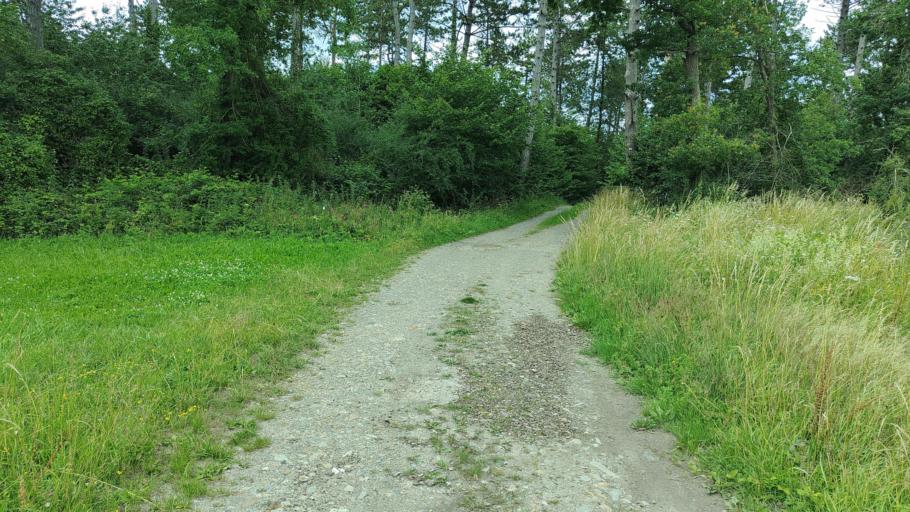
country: BE
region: Wallonia
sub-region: Province de Namur
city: Couvin
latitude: 50.0589
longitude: 4.4149
